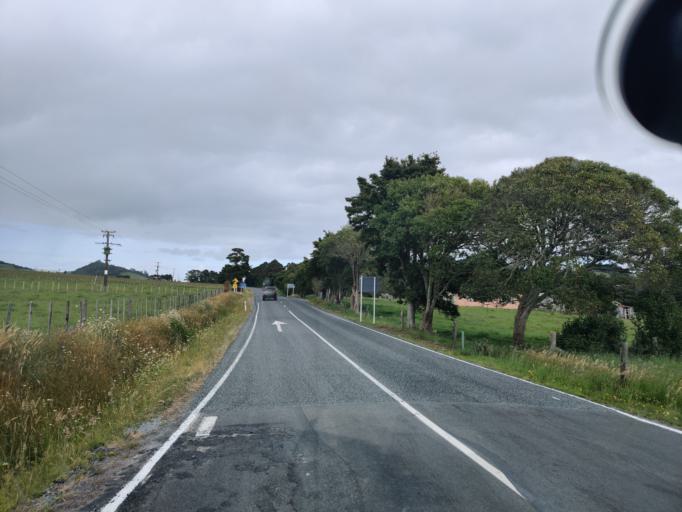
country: NZ
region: Northland
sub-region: Whangarei
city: Ngunguru
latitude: -35.5631
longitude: 174.3911
